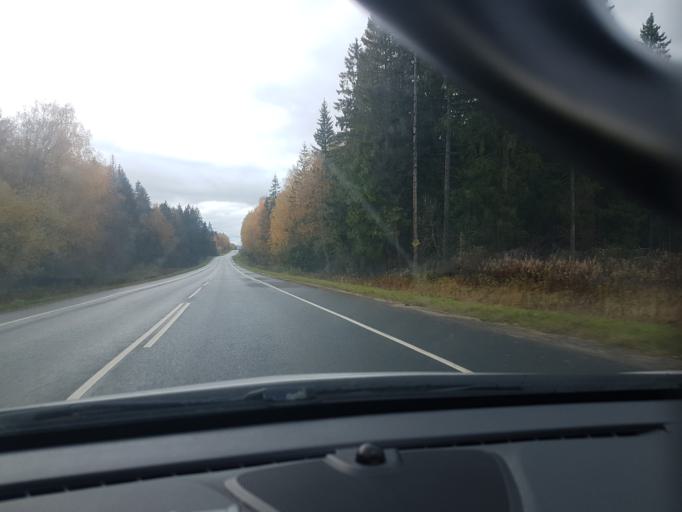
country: RU
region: Moskovskaya
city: Sychevo
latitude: 56.0044
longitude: 36.2936
